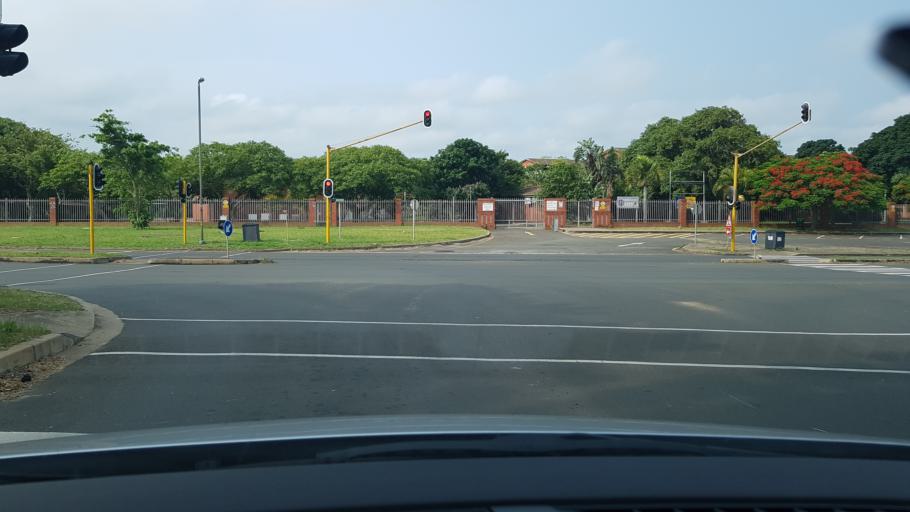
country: ZA
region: KwaZulu-Natal
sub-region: uThungulu District Municipality
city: Richards Bay
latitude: -28.7620
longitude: 32.0553
